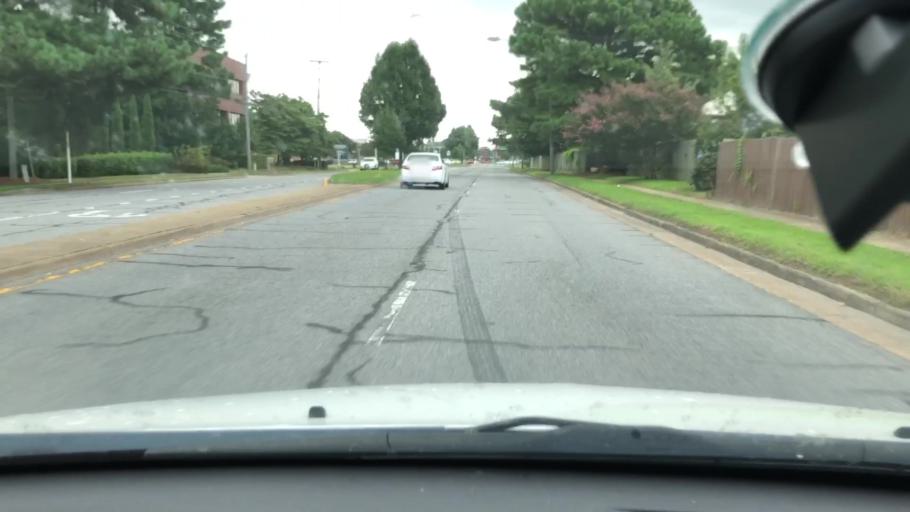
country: US
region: Virginia
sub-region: City of Chesapeake
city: Chesapeake
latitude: 36.8150
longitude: -76.1743
